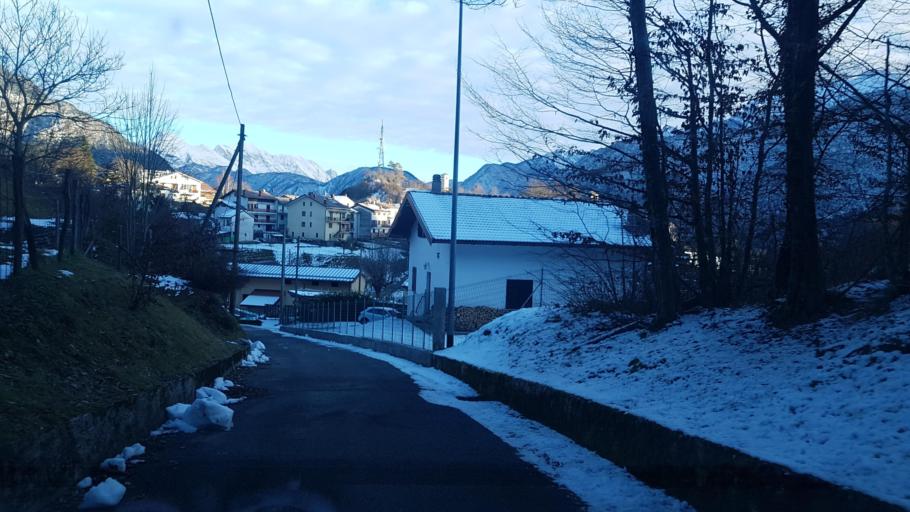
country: IT
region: Friuli Venezia Giulia
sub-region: Provincia di Udine
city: Moggio di Sotto
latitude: 46.4075
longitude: 13.1836
